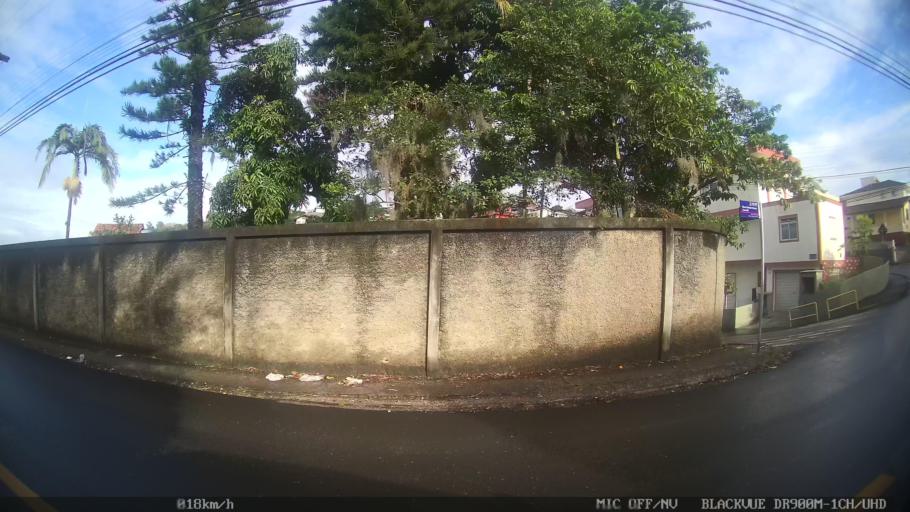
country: BR
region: Santa Catarina
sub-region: Sao Jose
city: Campinas
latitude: -27.6138
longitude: -48.6305
